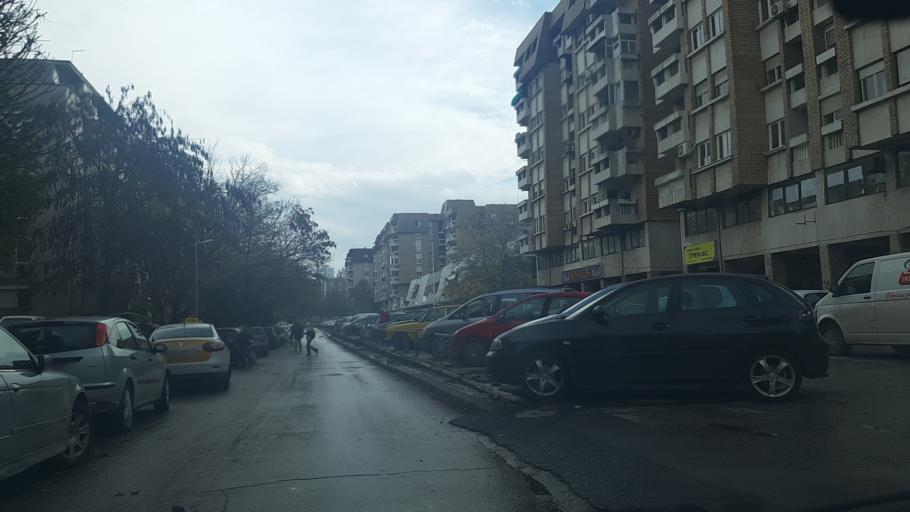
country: MK
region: Karpos
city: Skopje
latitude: 41.9900
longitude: 21.4498
